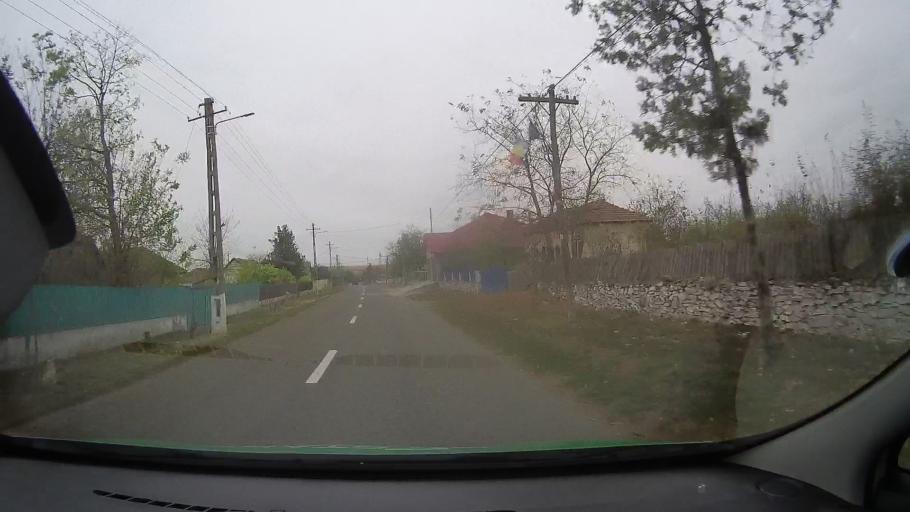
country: RO
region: Constanta
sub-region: Comuna Vulturu
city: Vulturu
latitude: 44.7019
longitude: 28.2386
